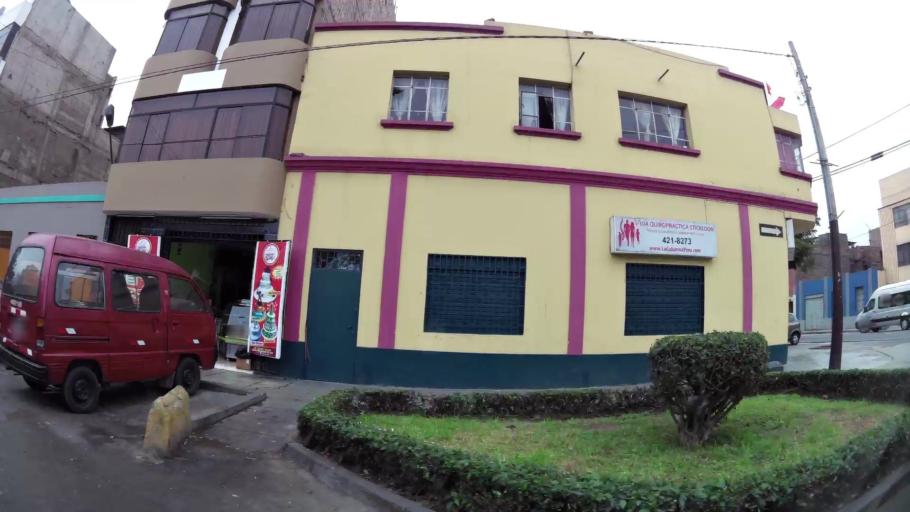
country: PE
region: Lima
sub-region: Lima
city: San Isidro
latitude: -12.0886
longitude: -77.0309
